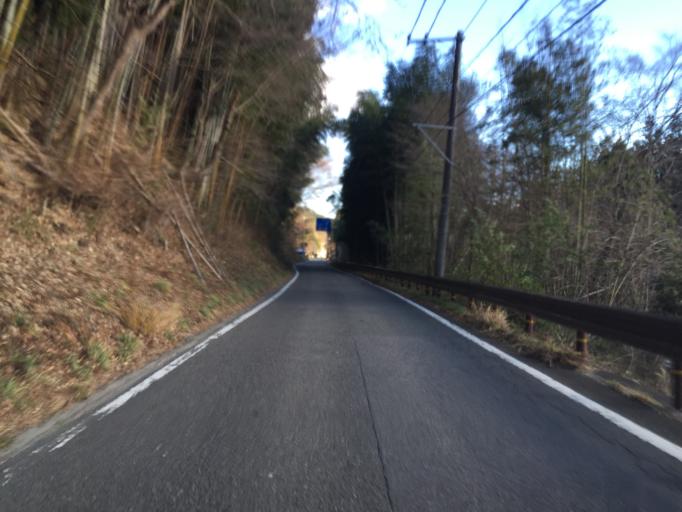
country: JP
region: Fukushima
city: Iwaki
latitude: 37.2089
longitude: 140.7441
